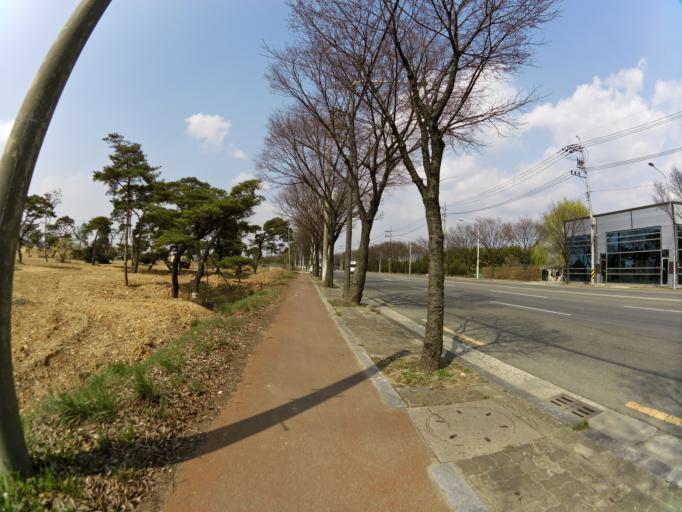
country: KR
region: Gyeongsangbuk-do
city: Gyeongsan-si
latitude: 35.8567
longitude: 128.7209
